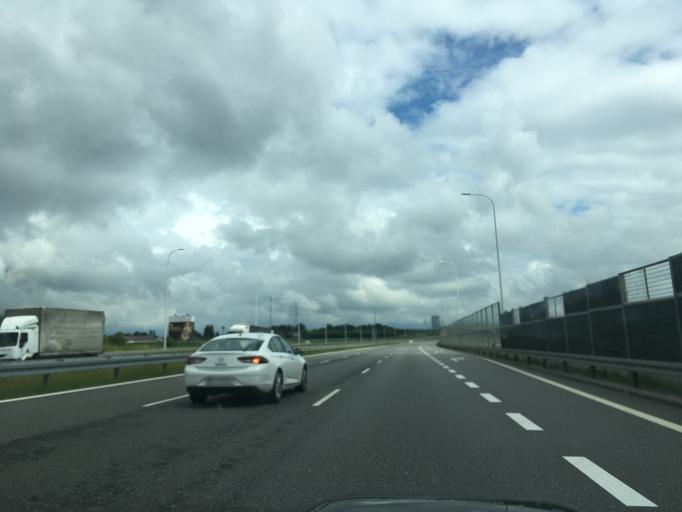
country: PL
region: Lublin Voivodeship
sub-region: Powiat lubelski
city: Lublin
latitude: 51.3017
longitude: 22.5660
